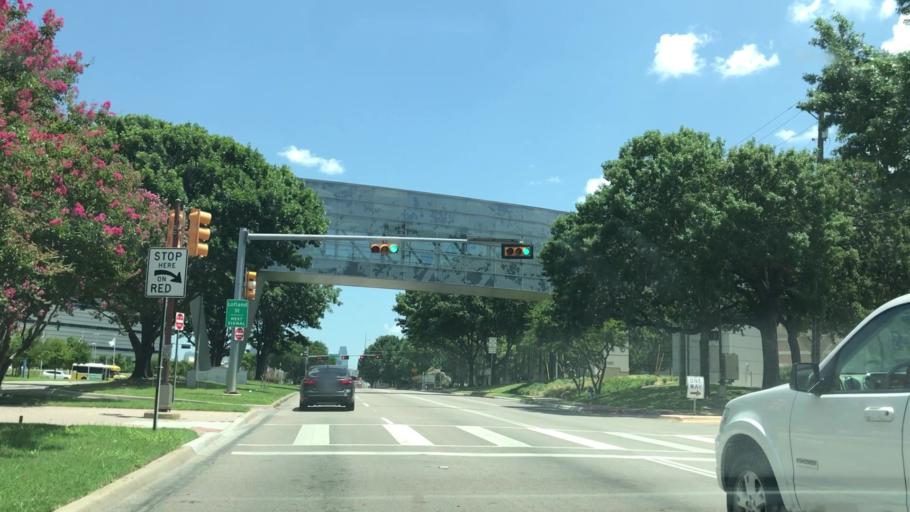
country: US
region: Texas
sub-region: Dallas County
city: Dallas
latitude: 32.8124
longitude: -96.8381
